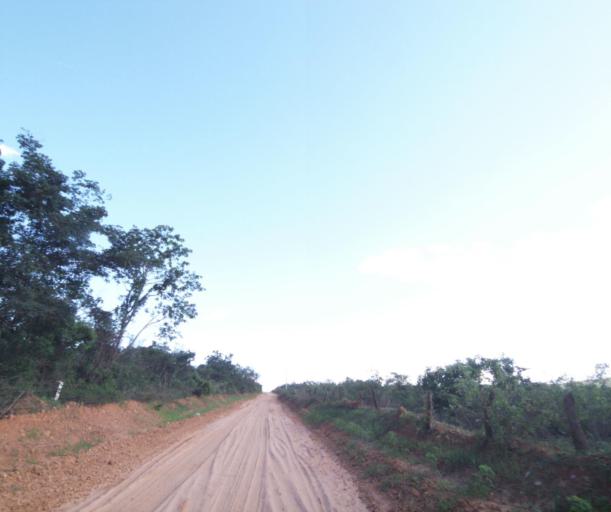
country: BR
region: Bahia
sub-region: Carinhanha
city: Carinhanha
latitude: -14.2252
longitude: -44.5336
